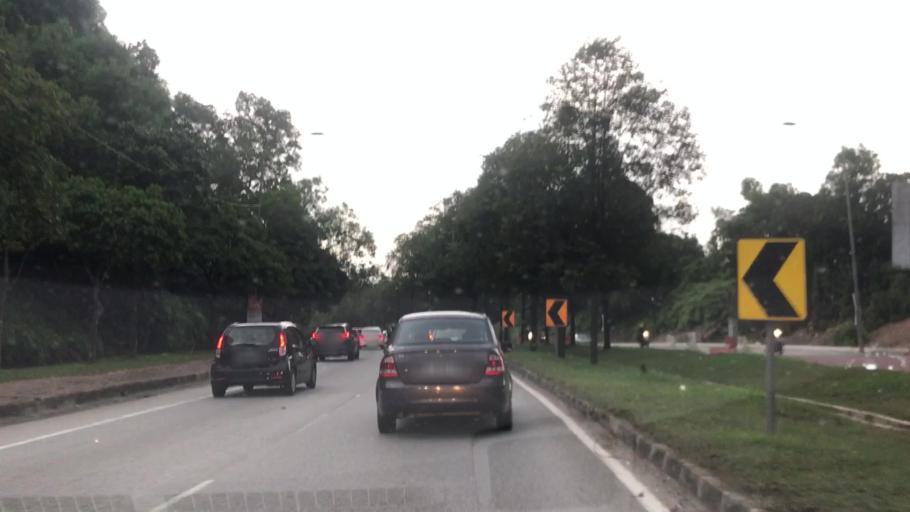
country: MY
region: Selangor
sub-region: Petaling
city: Petaling Jaya
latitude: 3.0557
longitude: 101.6659
